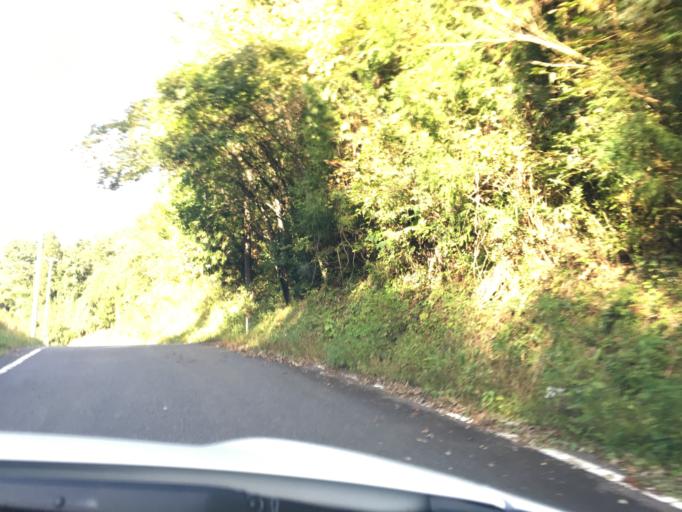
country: JP
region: Fukushima
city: Ishikawa
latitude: 37.1358
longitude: 140.5455
